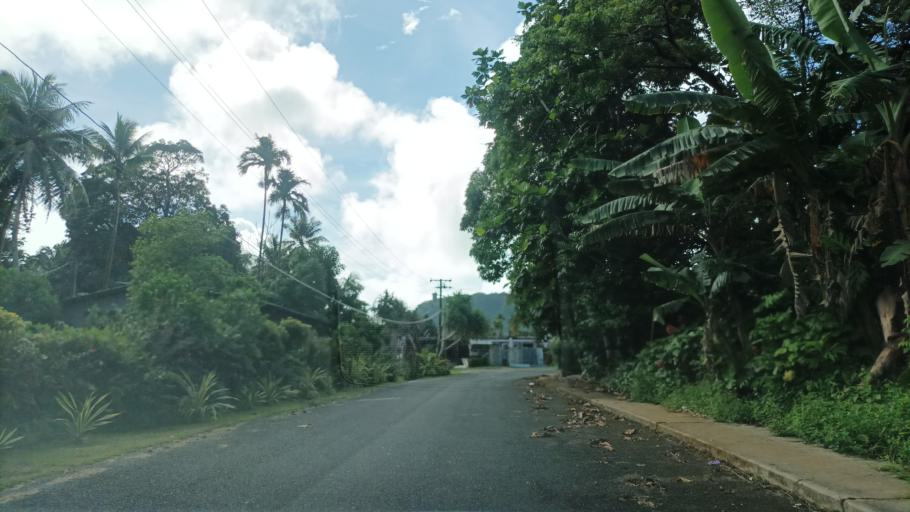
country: FM
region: Pohnpei
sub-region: Kolonia Municipality
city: Kolonia
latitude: 6.9610
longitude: 158.2075
